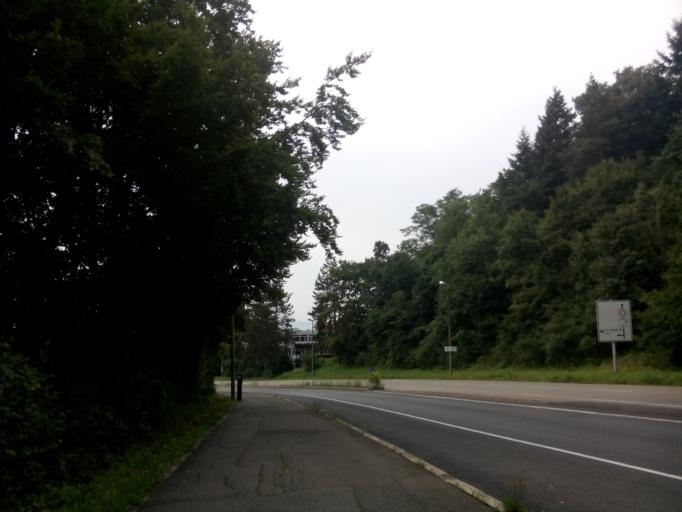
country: DE
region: Baden-Wuerttemberg
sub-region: Tuebingen Region
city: Tuebingen
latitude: 48.5298
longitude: 9.0448
